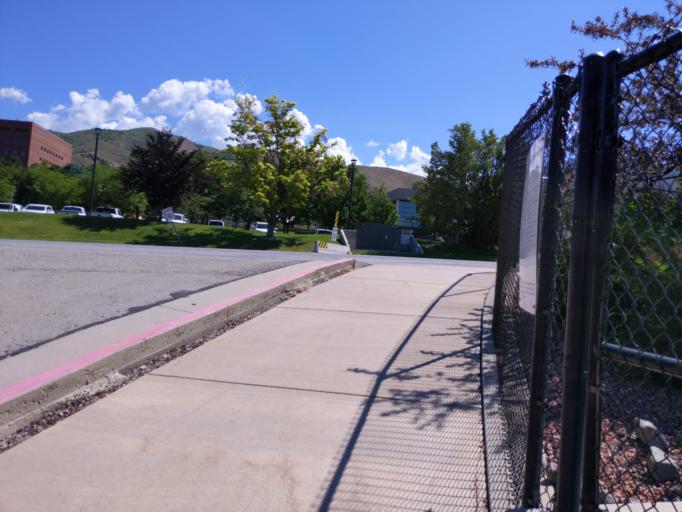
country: US
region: Utah
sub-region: Salt Lake County
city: Salt Lake City
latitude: 40.7673
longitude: -111.8392
